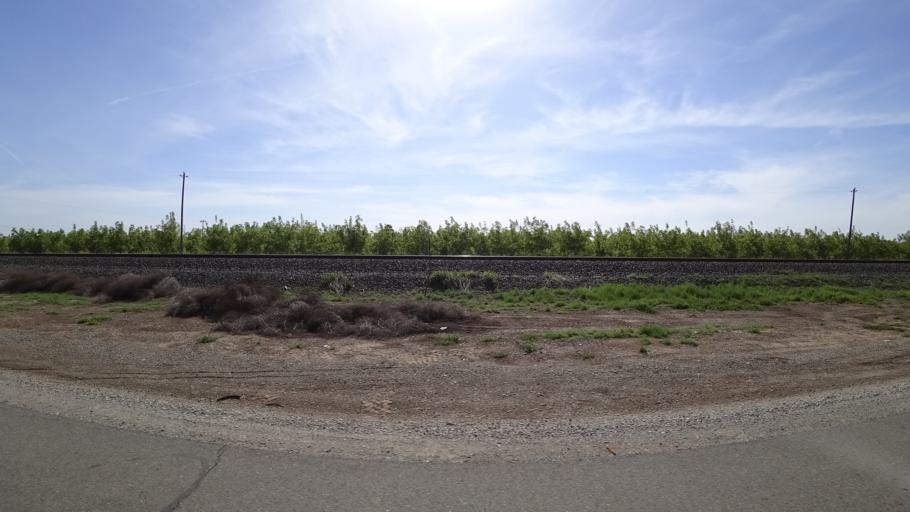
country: US
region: California
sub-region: Tehama County
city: Los Molinos
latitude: 40.0046
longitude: -122.0916
